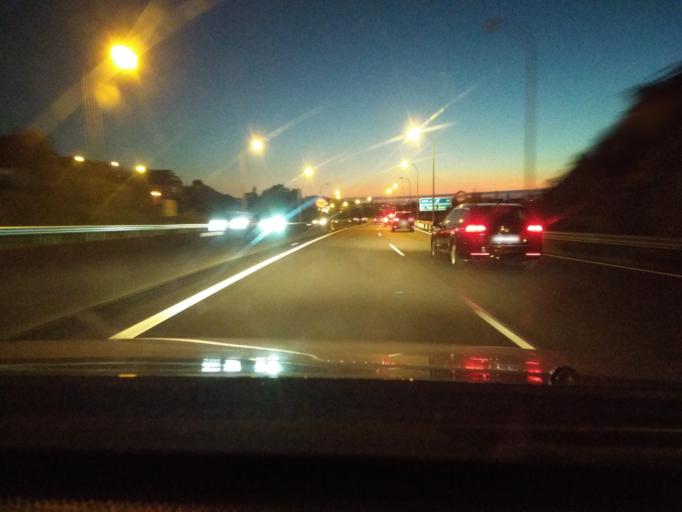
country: ES
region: Galicia
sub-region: Provincia de Pontevedra
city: Vigo
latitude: 42.2555
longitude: -8.6801
